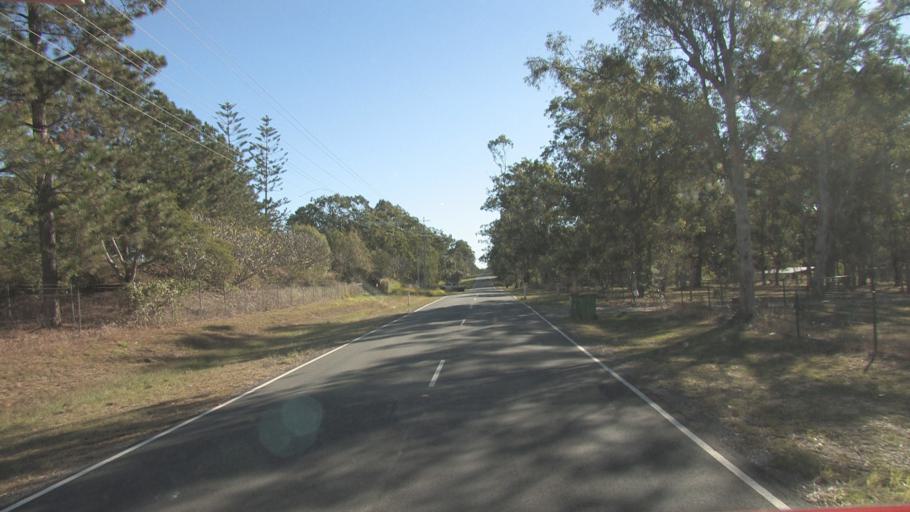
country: AU
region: Queensland
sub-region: Logan
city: Park Ridge South
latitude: -27.7367
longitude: 153.0243
